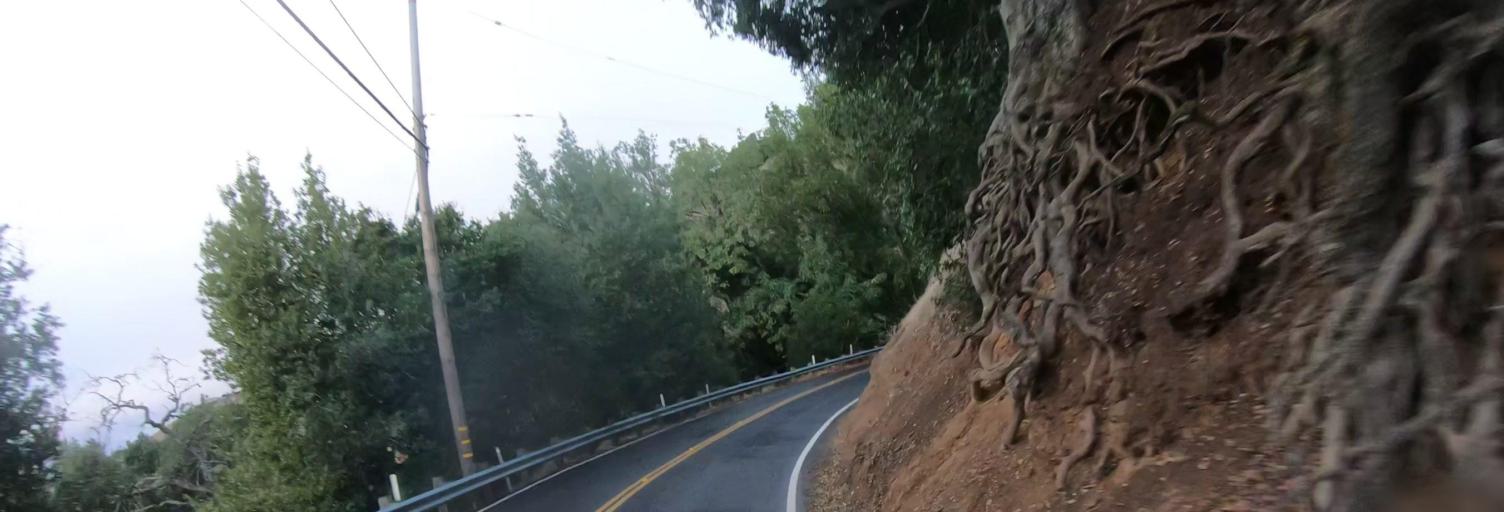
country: US
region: California
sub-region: Santa Clara County
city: East Foothills
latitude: 37.3302
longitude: -121.7481
